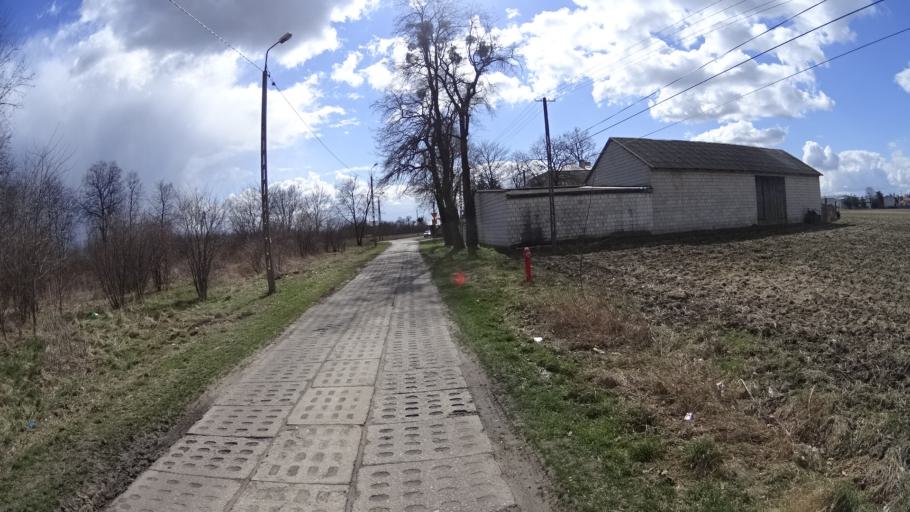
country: PL
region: Masovian Voivodeship
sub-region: Powiat warszawski zachodni
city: Jozefow
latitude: 52.2159
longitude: 20.7152
